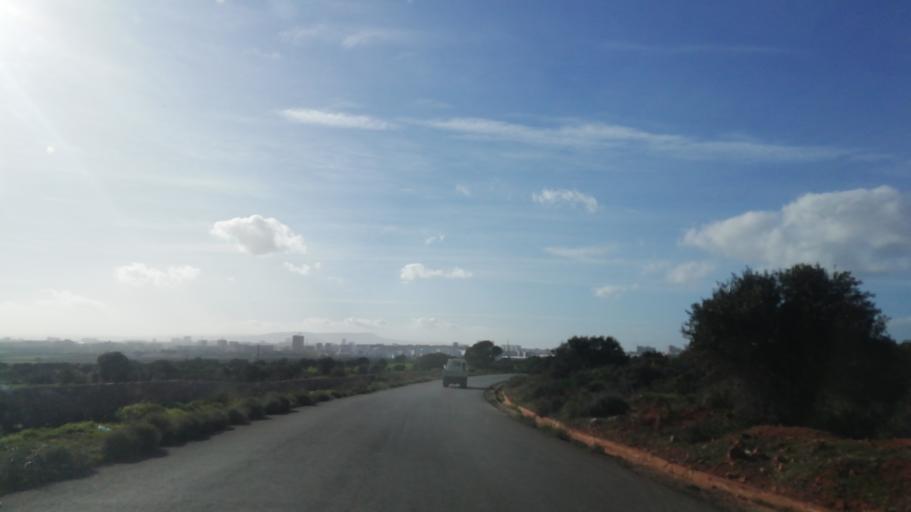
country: DZ
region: Oran
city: Bir el Djir
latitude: 35.7512
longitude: -0.5096
